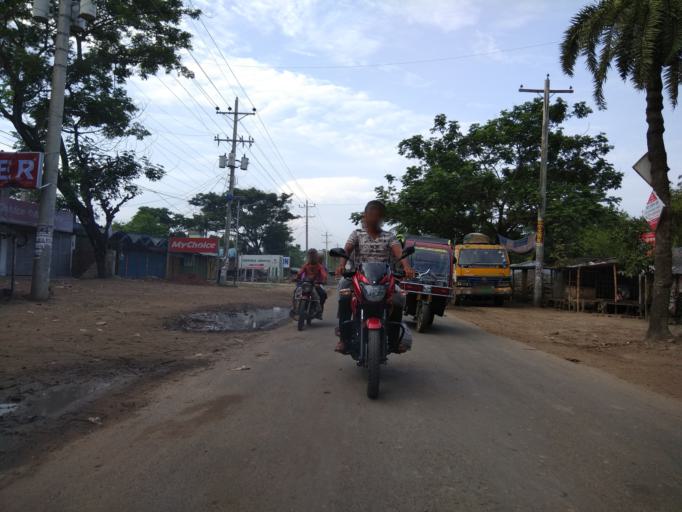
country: IN
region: West Bengal
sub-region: North 24 Parganas
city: Taki
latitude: 22.3425
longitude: 89.1051
